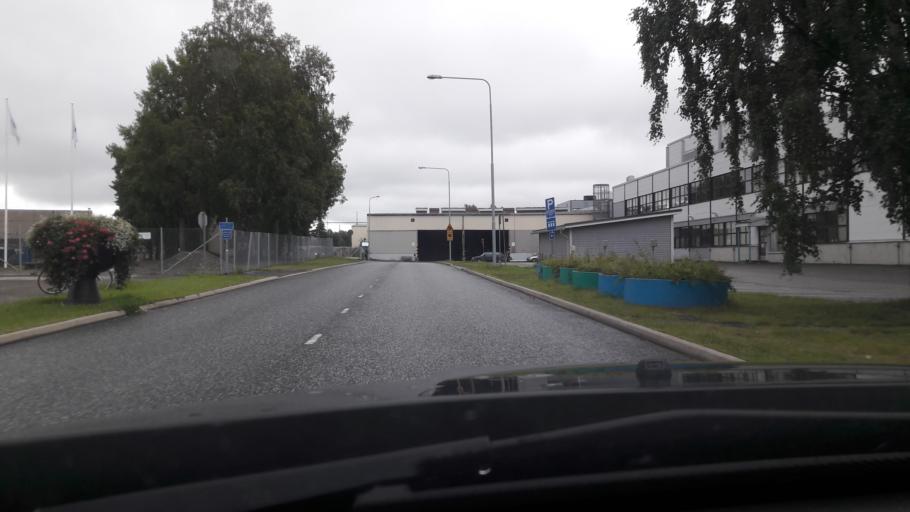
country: FI
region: North Karelia
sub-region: Joensuu
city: Joensuu
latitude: 62.6033
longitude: 29.7750
